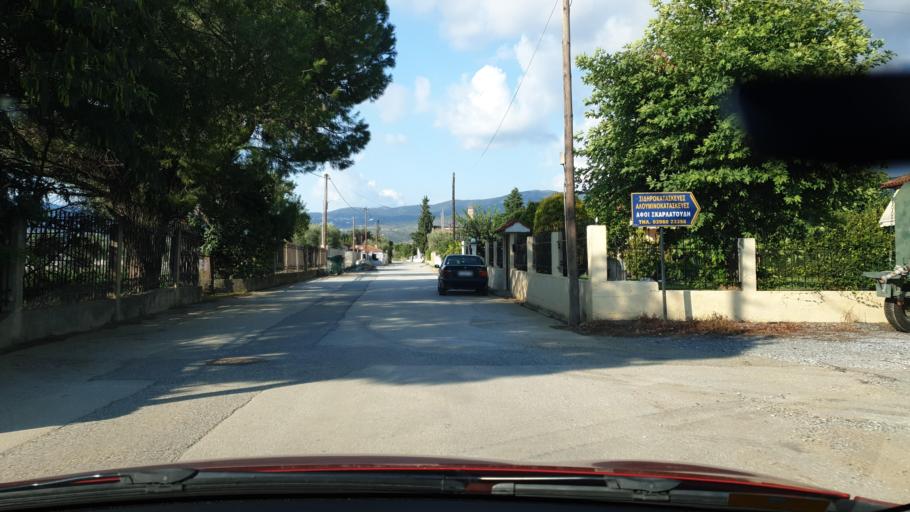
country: GR
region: Central Macedonia
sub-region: Nomos Thessalonikis
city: Vasilika
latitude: 40.4898
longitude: 23.1393
